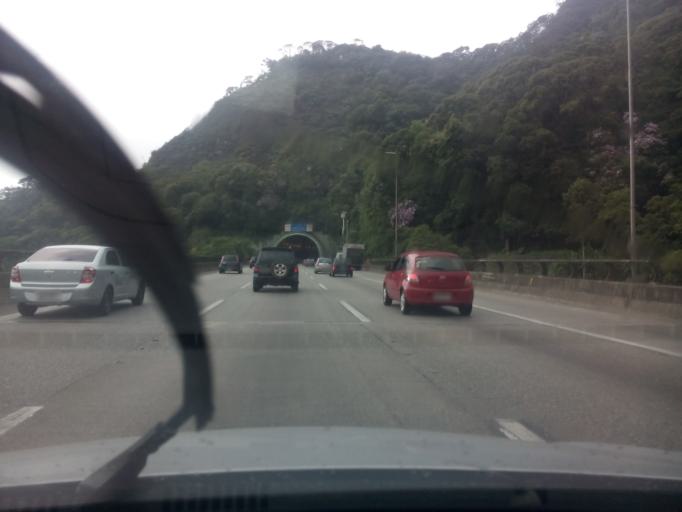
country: BR
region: Sao Paulo
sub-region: Cubatao
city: Cubatao
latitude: -23.9011
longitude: -46.5062
